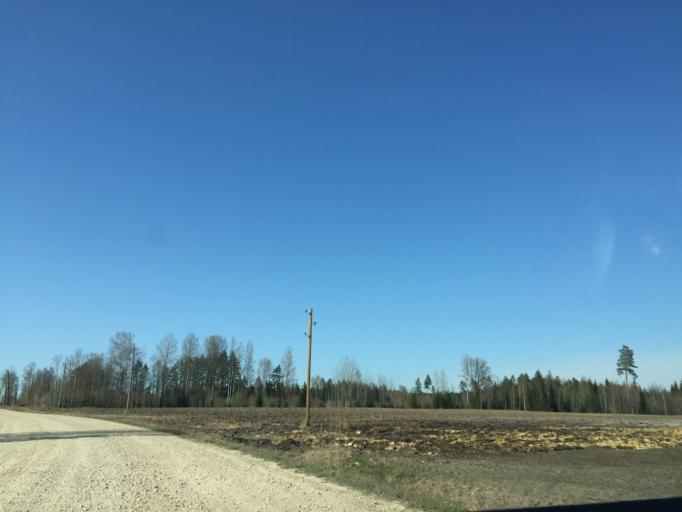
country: LV
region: Ropazu
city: Ropazi
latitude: 56.9442
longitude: 24.7024
